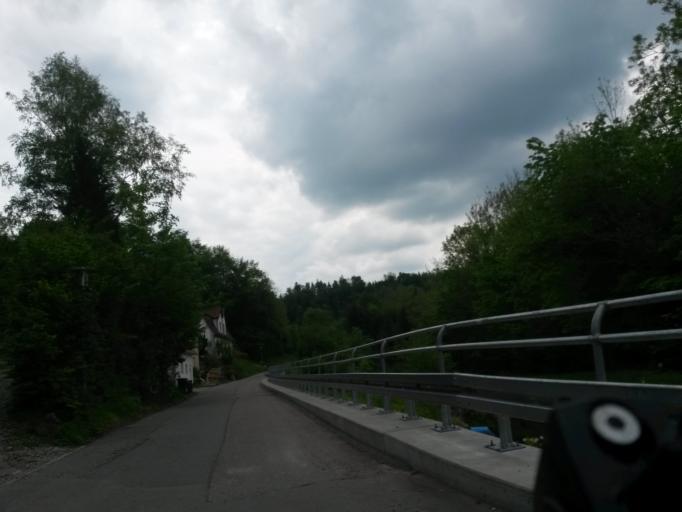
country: DE
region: Baden-Wuerttemberg
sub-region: Tuebingen Region
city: Wolfegg
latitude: 47.8379
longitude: 9.7865
